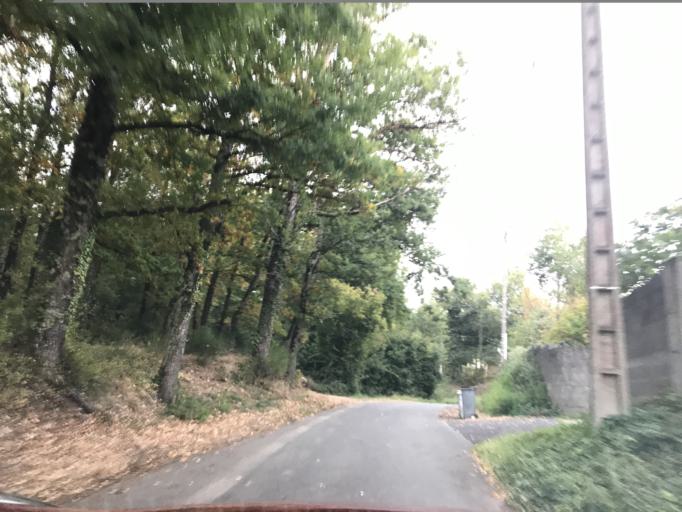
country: FR
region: Auvergne
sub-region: Departement du Puy-de-Dome
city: Thiers
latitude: 45.8434
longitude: 3.5420
